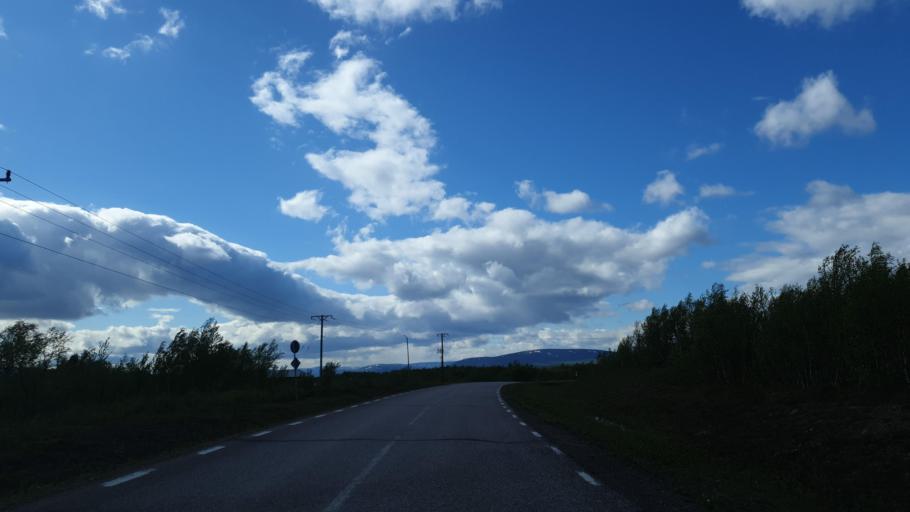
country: SE
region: Norrbotten
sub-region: Kiruna Kommun
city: Kiruna
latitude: 67.7669
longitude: 19.9837
